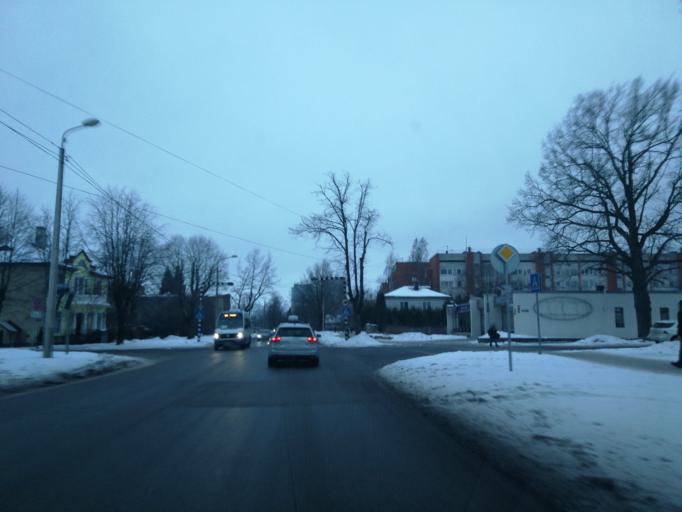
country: LV
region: Riga
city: Riga
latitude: 56.9490
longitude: 24.1726
